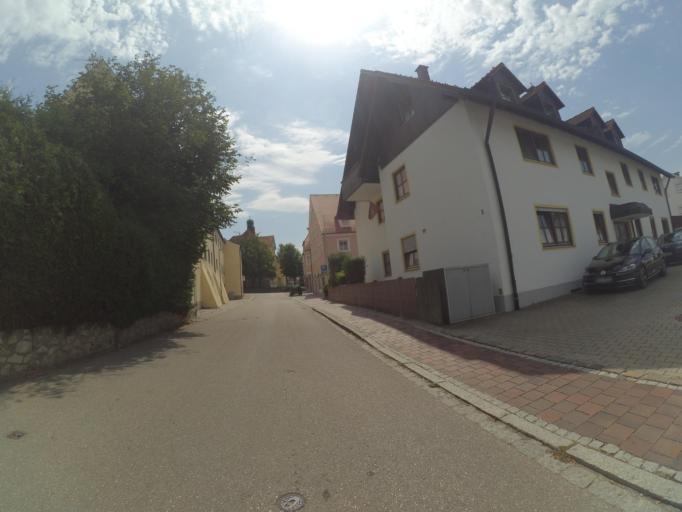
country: DE
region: Bavaria
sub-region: Swabia
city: Buchloe
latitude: 48.0381
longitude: 10.7283
